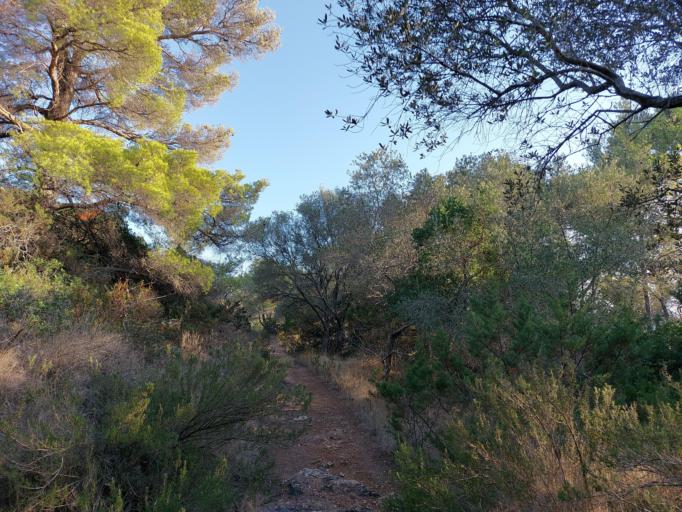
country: HR
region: Dubrovacko-Neretvanska
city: Smokvica
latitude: 42.7716
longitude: 16.7886
